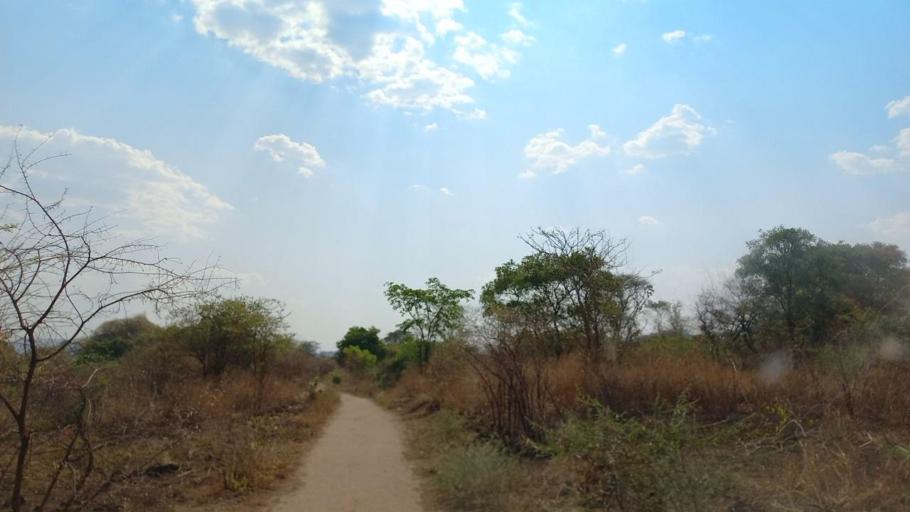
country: ZM
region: Lusaka
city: Luangwa
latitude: -15.0907
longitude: 30.1532
